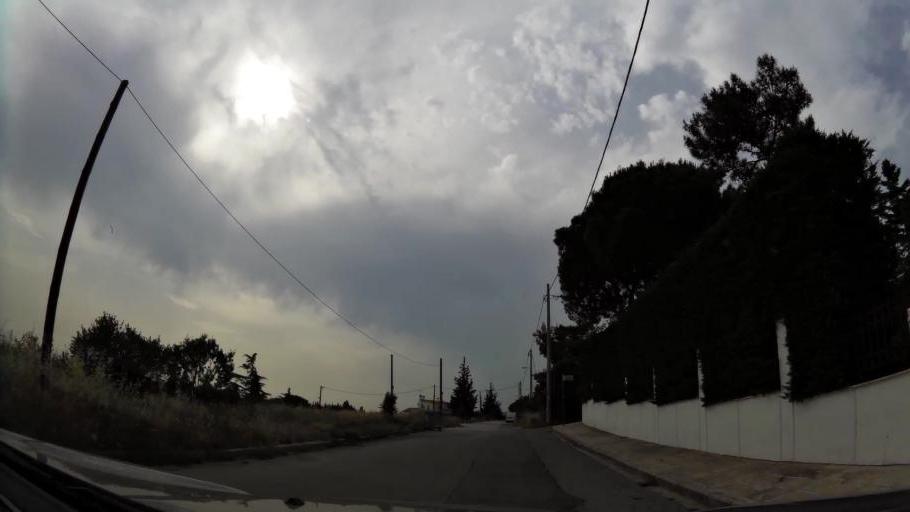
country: GR
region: Central Macedonia
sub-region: Nomos Thessalonikis
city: Oraiokastro
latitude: 40.7112
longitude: 22.9245
